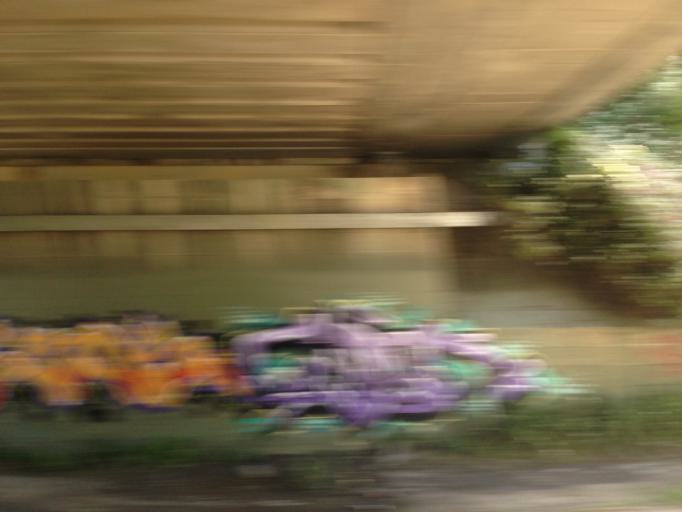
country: AU
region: New South Wales
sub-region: North Sydney
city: St Leonards
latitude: -33.8175
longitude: 151.1933
